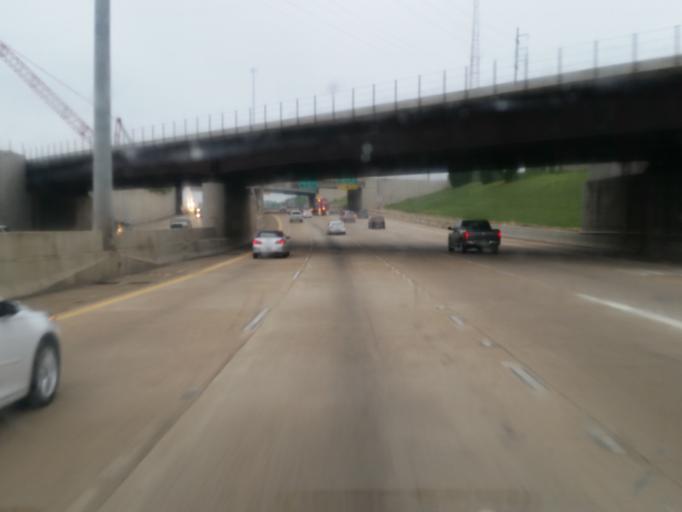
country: US
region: Louisiana
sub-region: Caddo Parish
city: Shreveport
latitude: 32.4988
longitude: -93.7544
